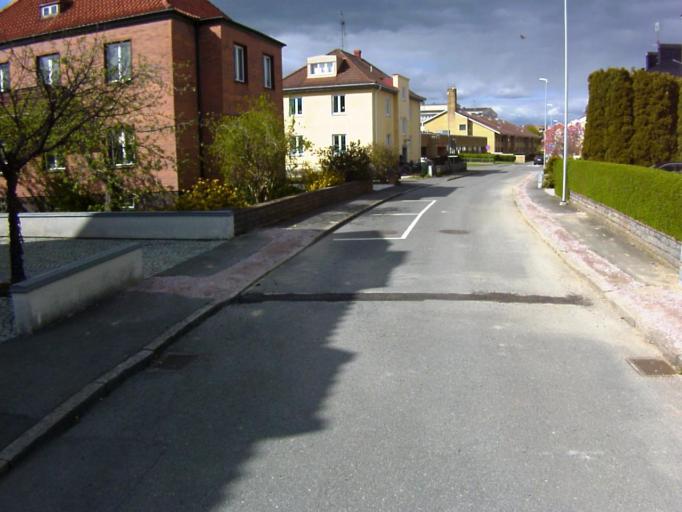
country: SE
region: Skane
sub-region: Kristianstads Kommun
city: Kristianstad
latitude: 56.0341
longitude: 14.1605
